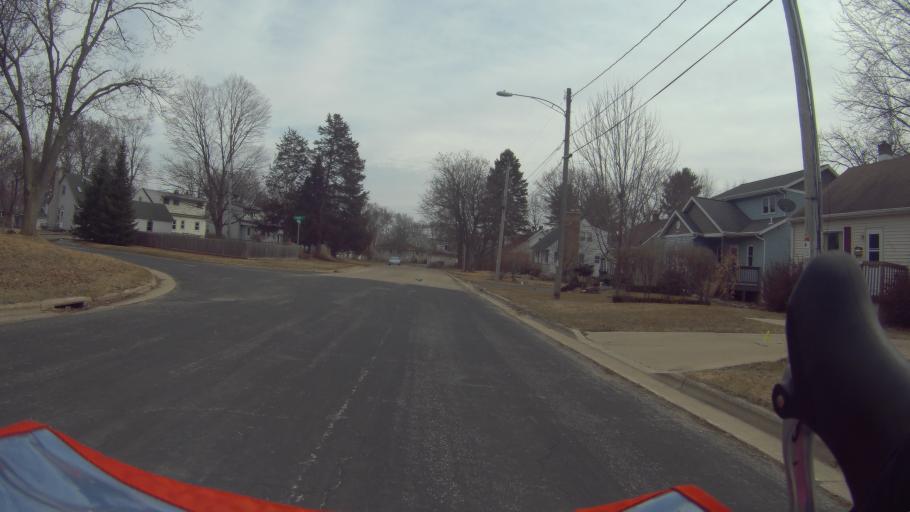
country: US
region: Wisconsin
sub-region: Dane County
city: Maple Bluff
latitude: 43.1166
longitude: -89.3671
